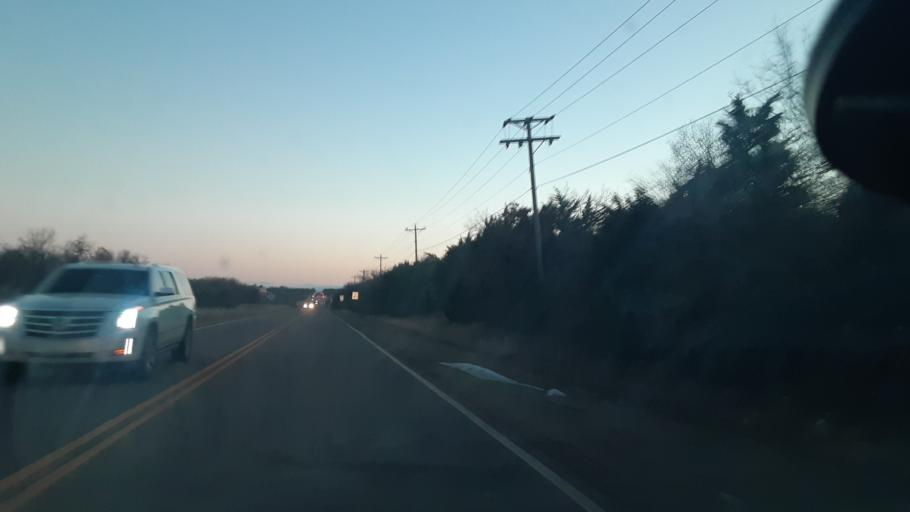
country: US
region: Oklahoma
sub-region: Oklahoma County
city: Edmond
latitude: 35.6965
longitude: -97.4251
